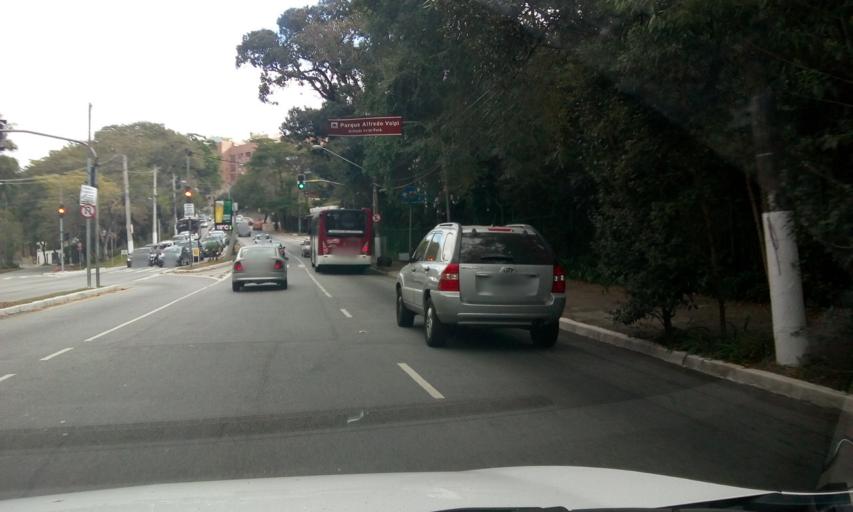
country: BR
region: Sao Paulo
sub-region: Sao Paulo
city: Sao Paulo
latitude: -23.5892
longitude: -46.7010
